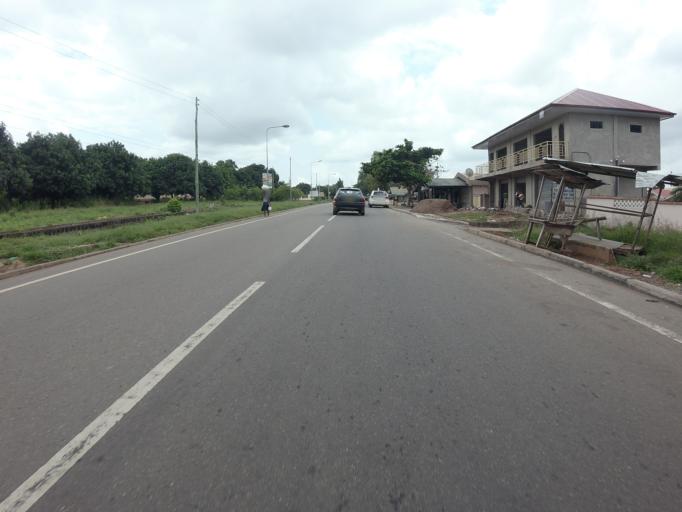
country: GH
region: Volta
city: Ho
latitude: 6.6117
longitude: 0.4847
